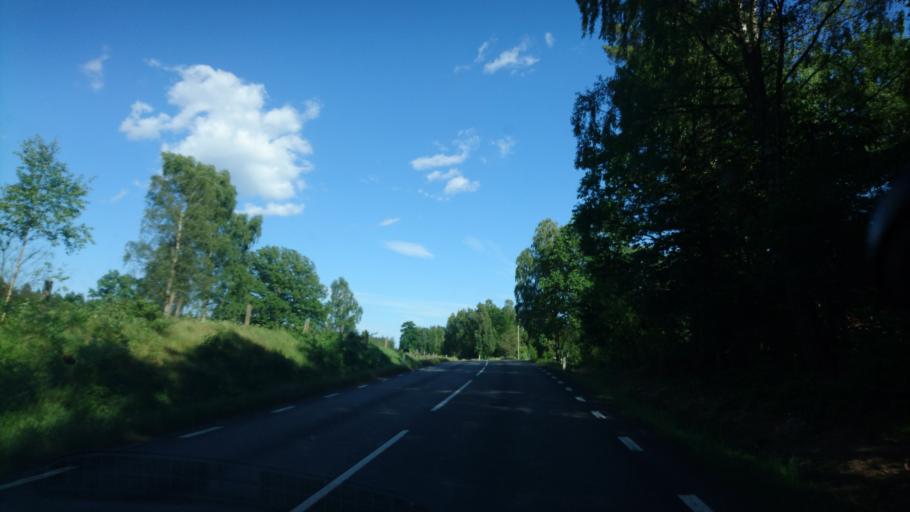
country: SE
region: Skane
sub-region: Osby Kommun
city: Lonsboda
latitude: 56.3917
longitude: 14.3913
